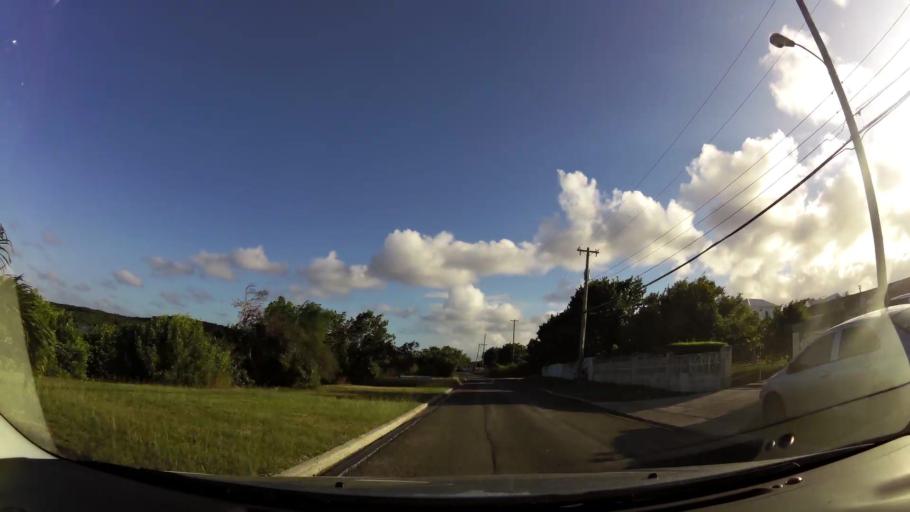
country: AG
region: Saint George
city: Piggotts
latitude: 17.1254
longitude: -61.7889
